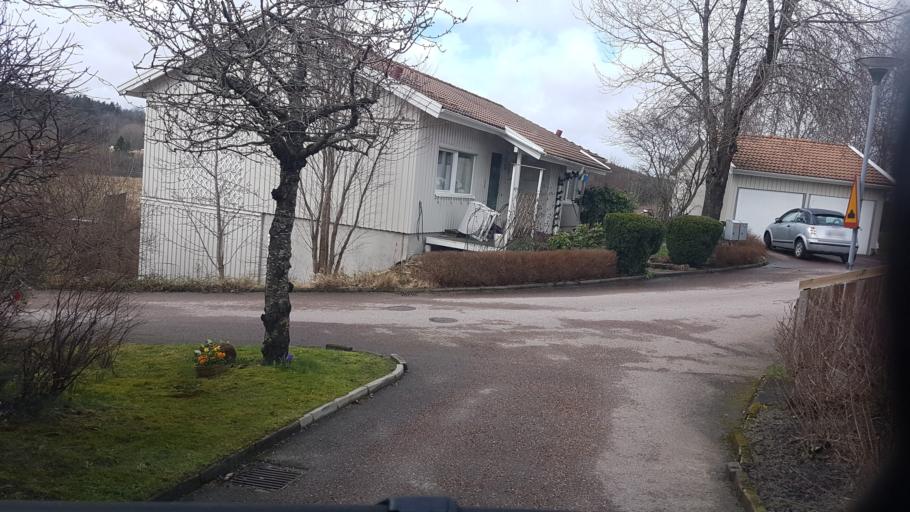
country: SE
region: Vaestra Goetaland
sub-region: Lerums Kommun
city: Stenkullen
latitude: 57.7893
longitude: 12.3008
